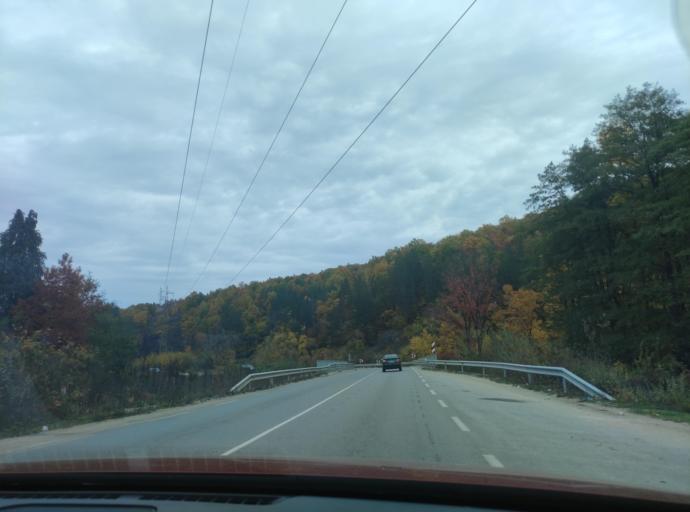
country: BG
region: Montana
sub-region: Obshtina Berkovitsa
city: Berkovitsa
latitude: 43.2615
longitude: 23.1778
